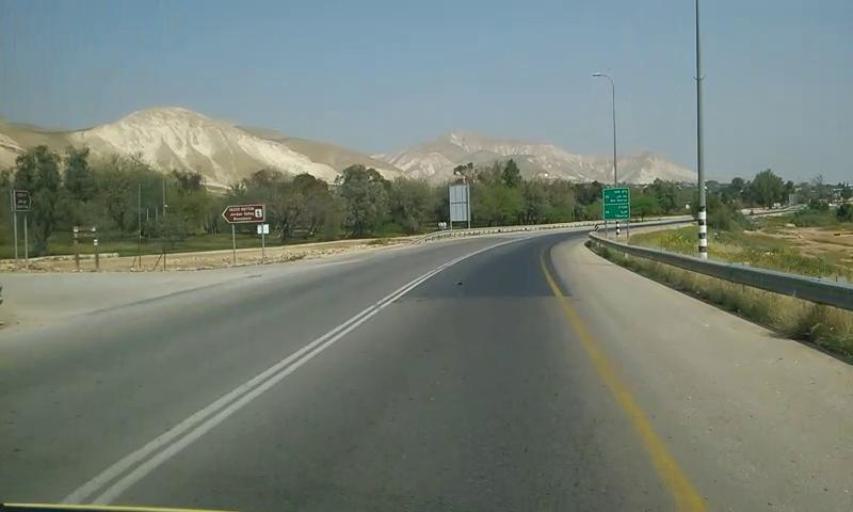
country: PS
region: West Bank
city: Al Fasayil
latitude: 32.0519
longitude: 35.4658
